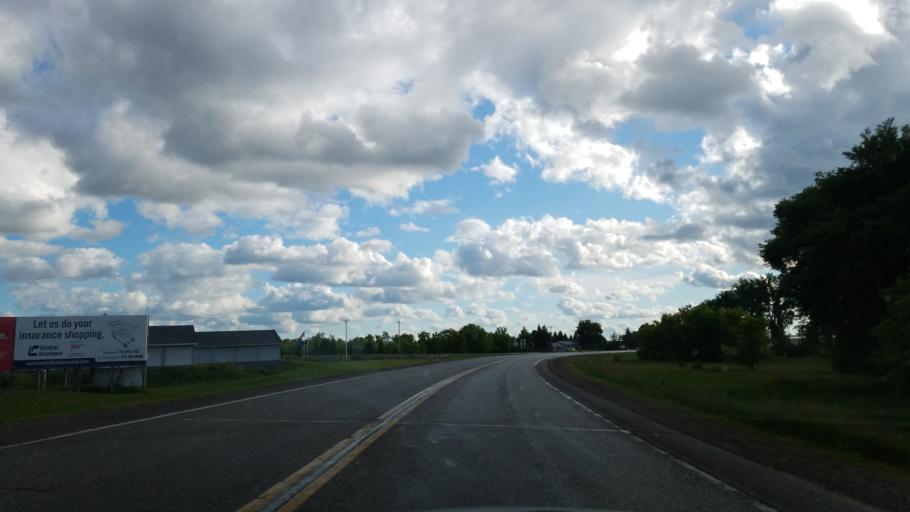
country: US
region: Wisconsin
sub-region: Polk County
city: Saint Croix Falls
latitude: 45.3448
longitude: -92.6422
